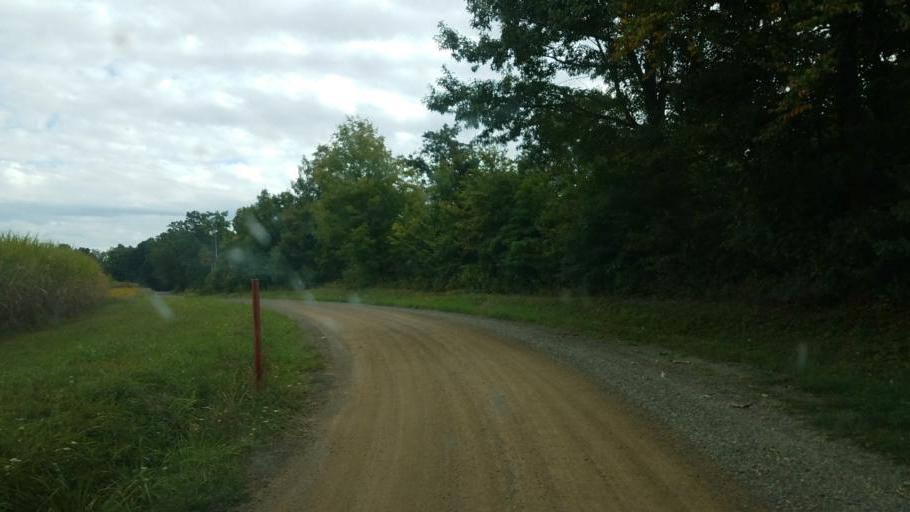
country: US
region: Pennsylvania
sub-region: Crawford County
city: Pymatuning Central
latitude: 41.5372
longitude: -80.4637
